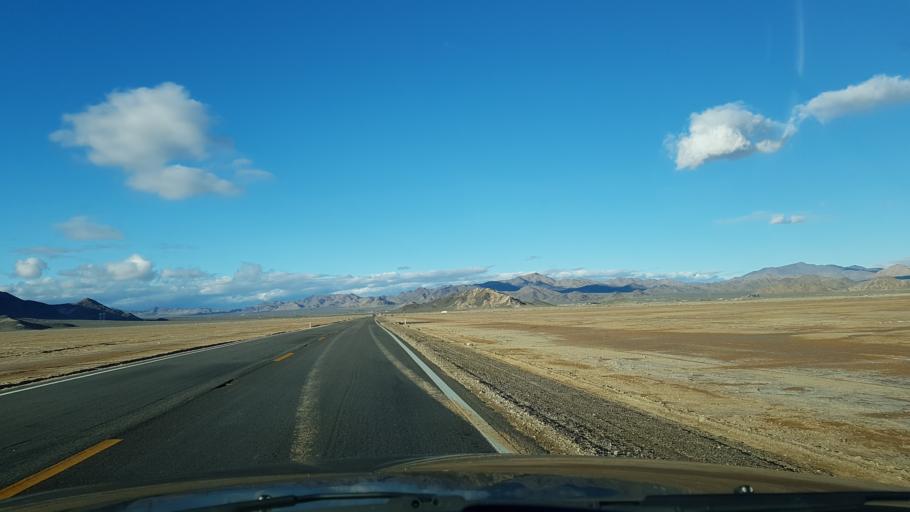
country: US
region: California
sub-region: San Bernardino County
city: Lucerne Valley
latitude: 34.5089
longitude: -116.9454
